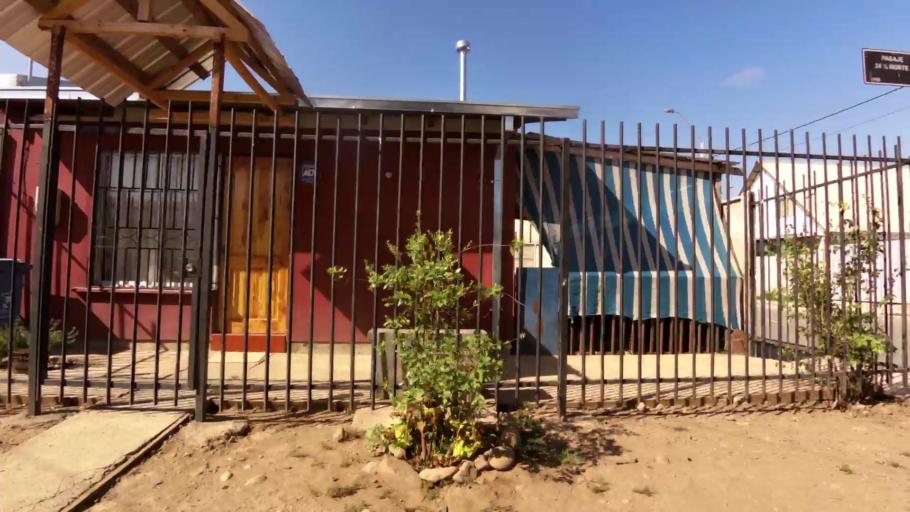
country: CL
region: Maule
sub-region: Provincia de Talca
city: Talca
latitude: -35.3919
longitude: -71.6526
